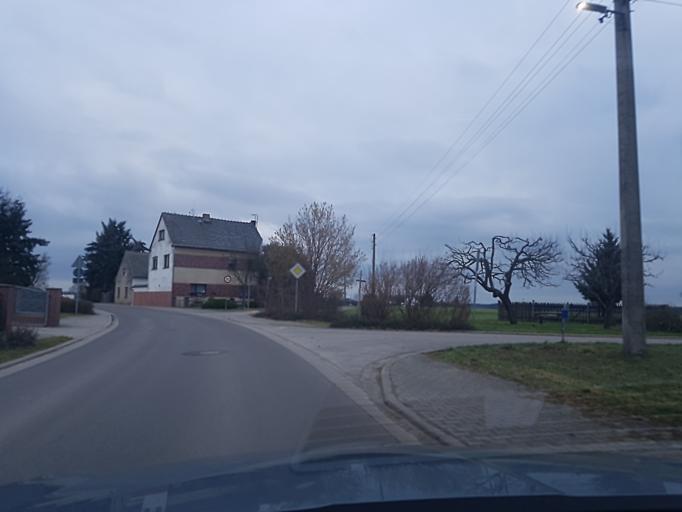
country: DE
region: Brandenburg
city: Sonnewalde
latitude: 51.6900
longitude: 13.6793
